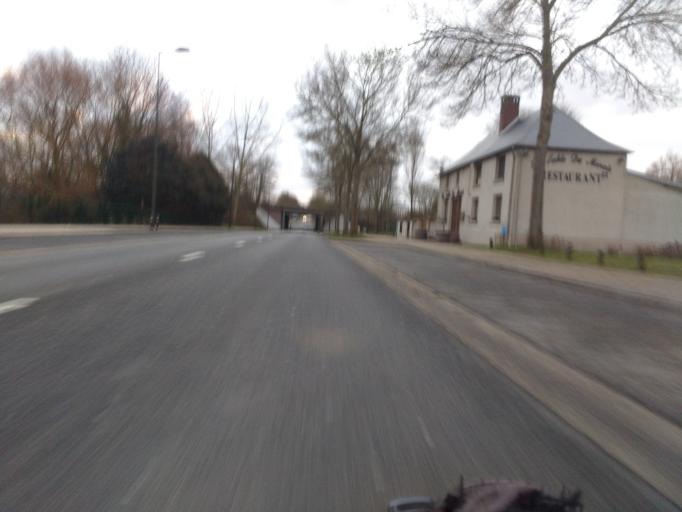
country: FR
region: Picardie
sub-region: Departement de la Somme
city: Camon
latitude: 49.8781
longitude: 2.3390
